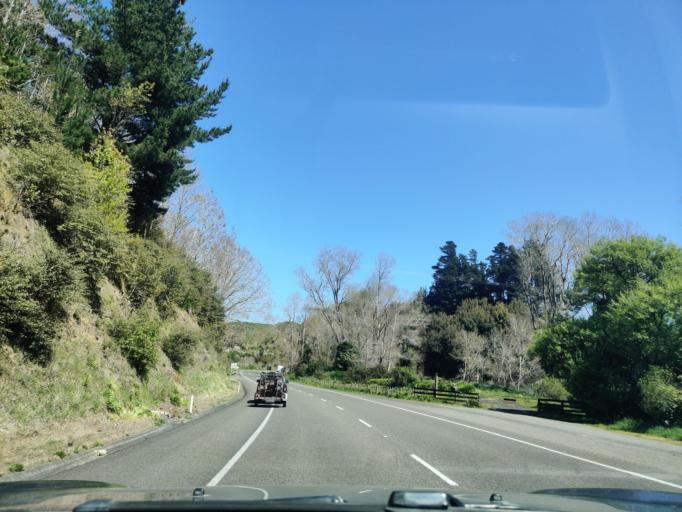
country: NZ
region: Manawatu-Wanganui
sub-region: Wanganui District
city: Wanganui
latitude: -39.8312
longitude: 174.8912
